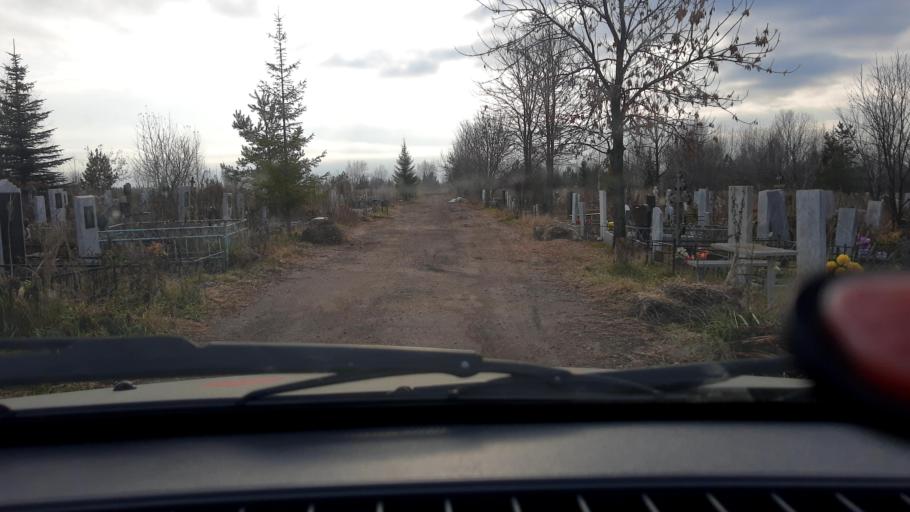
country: RU
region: Bashkortostan
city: Ufa
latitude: 54.8589
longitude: 56.1645
